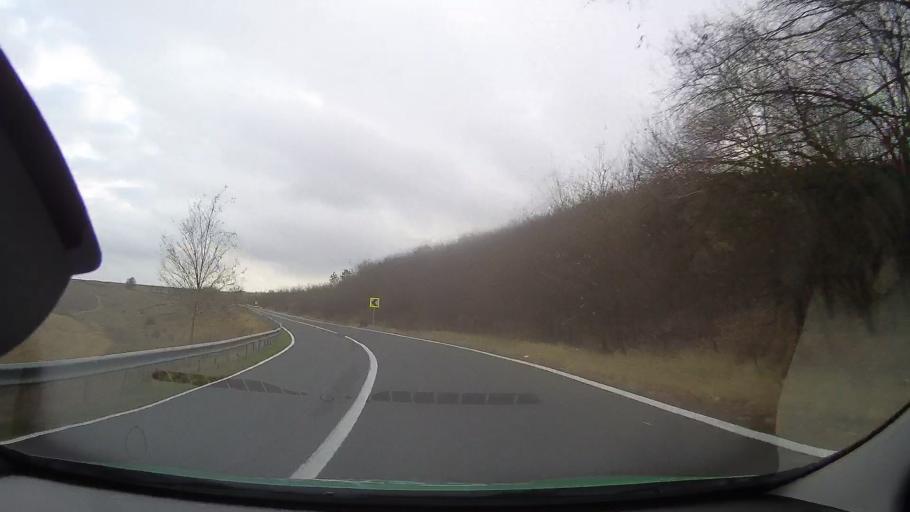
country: RO
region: Constanta
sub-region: Comuna Deleni
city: Deleni
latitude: 44.0989
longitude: 28.0187
